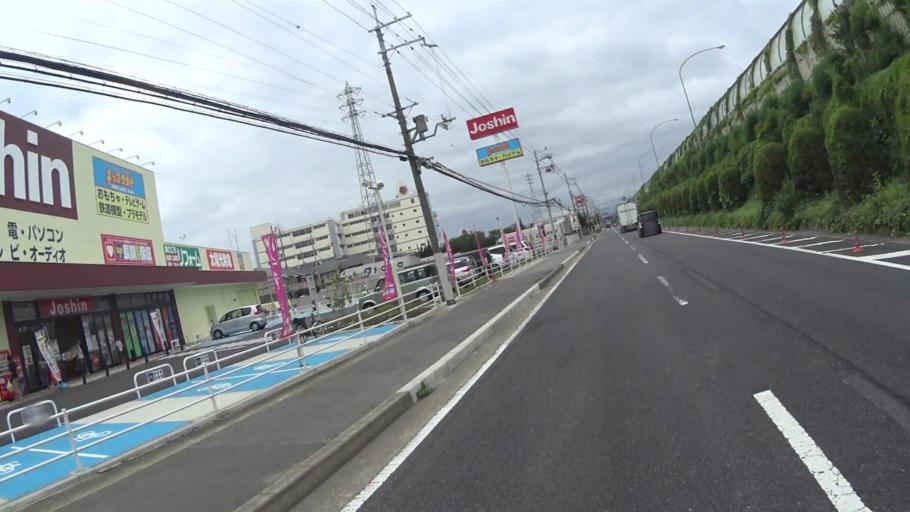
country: JP
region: Kyoto
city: Muko
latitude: 34.9242
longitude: 135.7107
